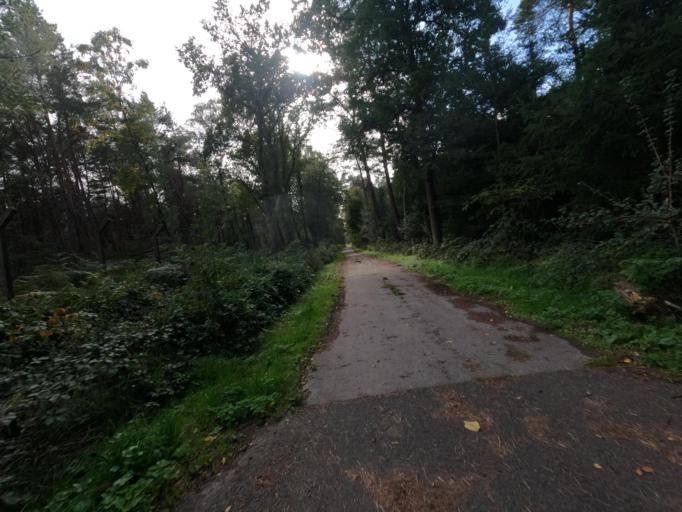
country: DE
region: North Rhine-Westphalia
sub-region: Regierungsbezirk Koln
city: Gangelt
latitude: 50.9739
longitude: 6.0503
